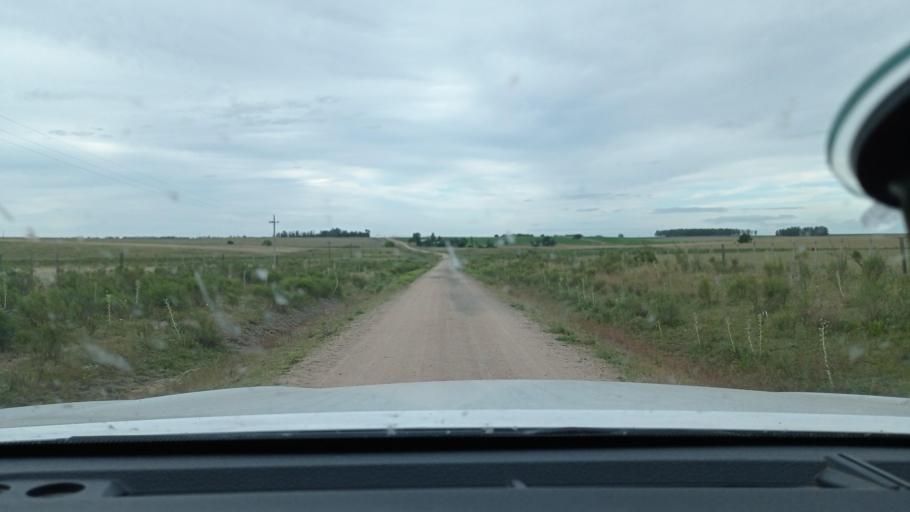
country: UY
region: Florida
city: Casupa
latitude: -34.1246
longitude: -55.7737
